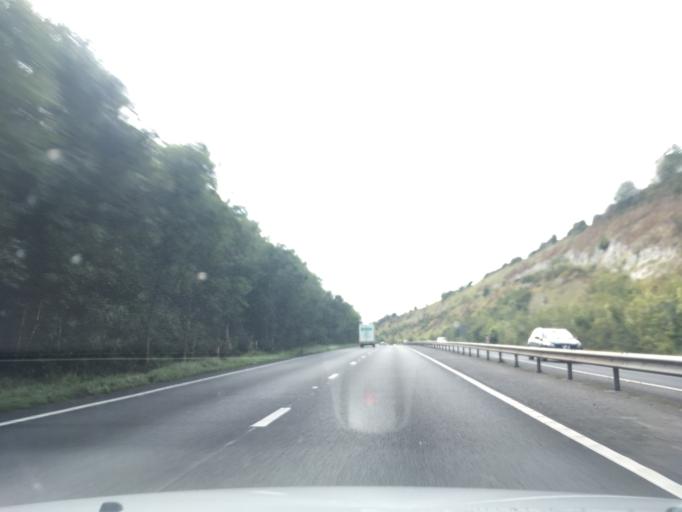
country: GB
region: England
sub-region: Hampshire
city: Petersfield
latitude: 50.9777
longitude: -0.9692
